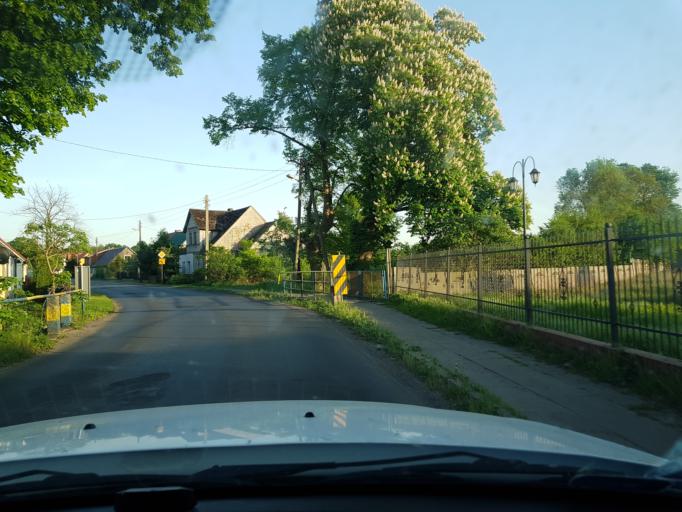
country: PL
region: West Pomeranian Voivodeship
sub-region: Powiat stargardzki
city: Kobylanka
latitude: 53.4204
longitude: 14.9038
